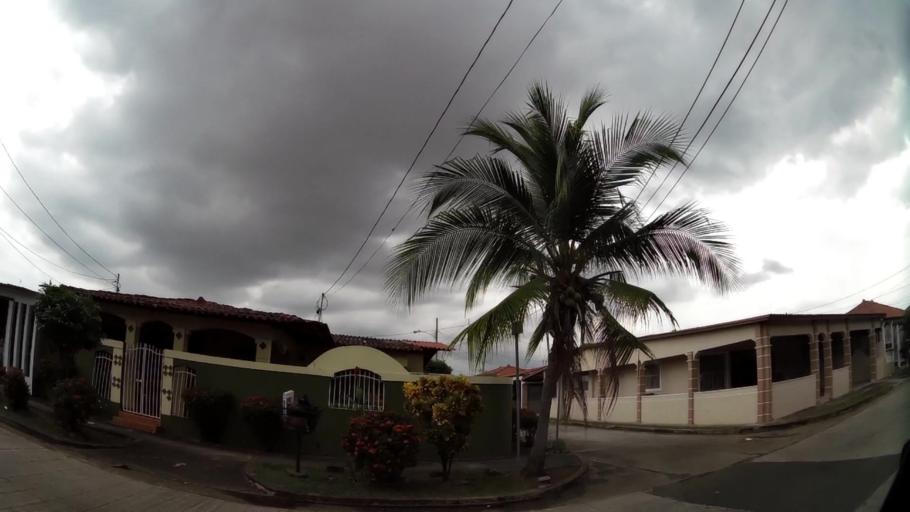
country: PA
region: Panama
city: Tocumen
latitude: 9.0495
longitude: -79.4116
